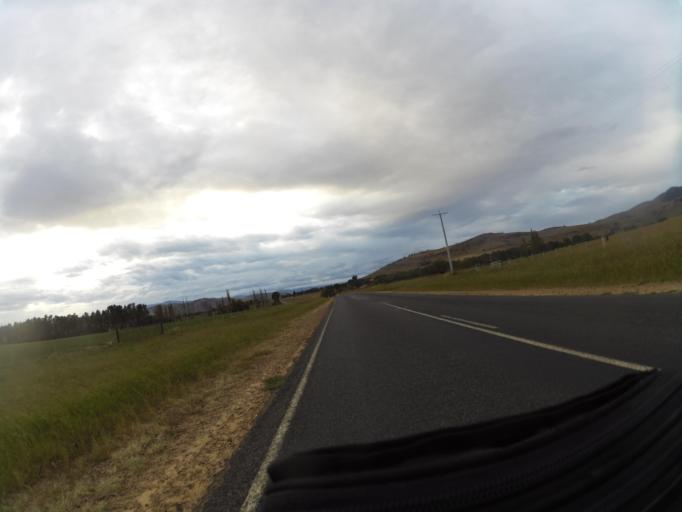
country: AU
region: New South Wales
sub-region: Greater Hume Shire
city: Holbrook
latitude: -36.0647
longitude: 147.9506
